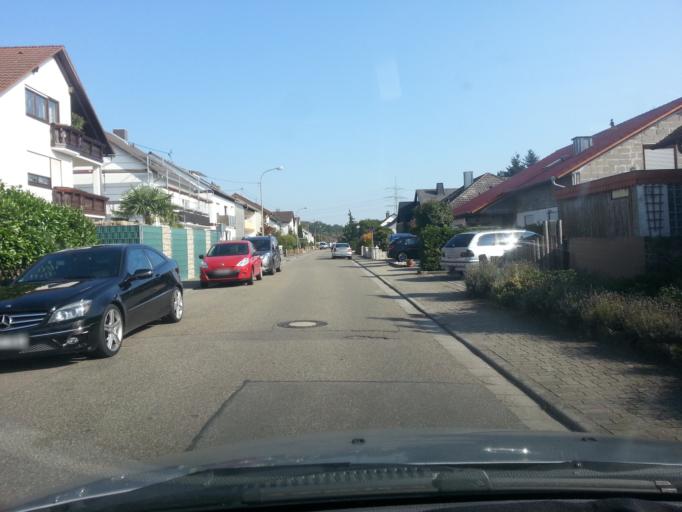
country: DE
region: Rheinland-Pfalz
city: Bohl-Iggelheim
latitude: 49.3576
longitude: 8.3155
